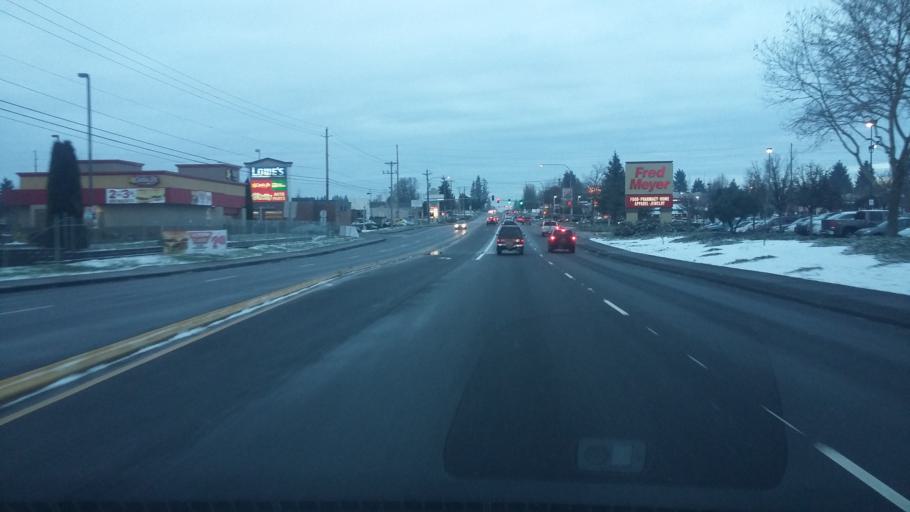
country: US
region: Washington
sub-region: Clark County
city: Orchards
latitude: 45.6757
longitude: -122.5525
